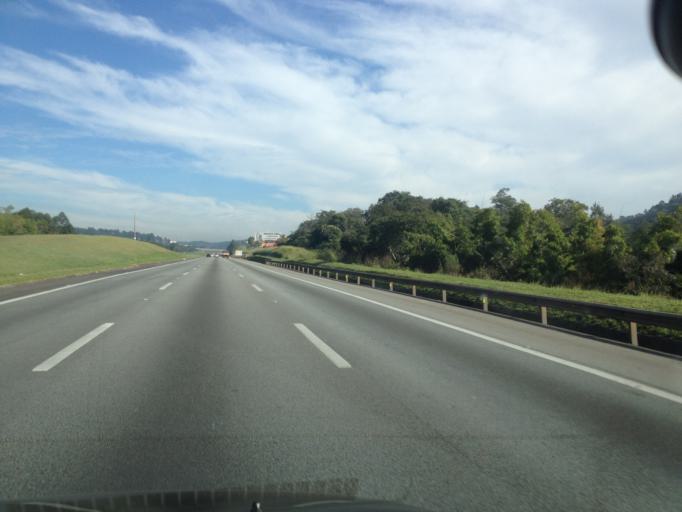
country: BR
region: Sao Paulo
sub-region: Sao Roque
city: Sao Roque
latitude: -23.4202
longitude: -47.1893
